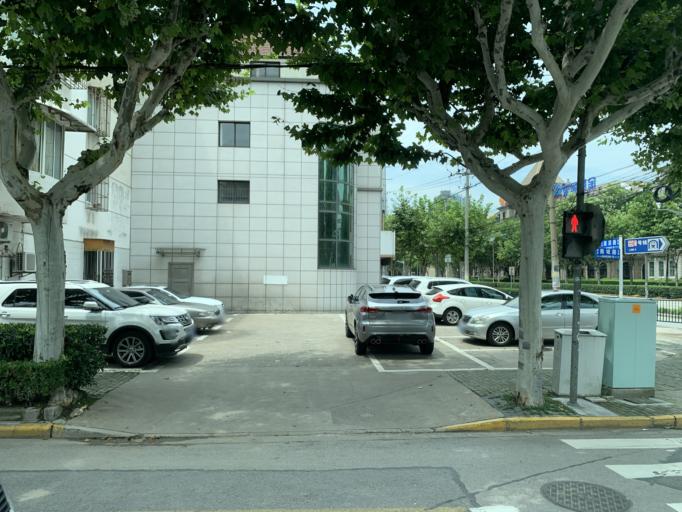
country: CN
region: Shanghai Shi
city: Pudong
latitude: 31.2384
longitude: 121.5273
